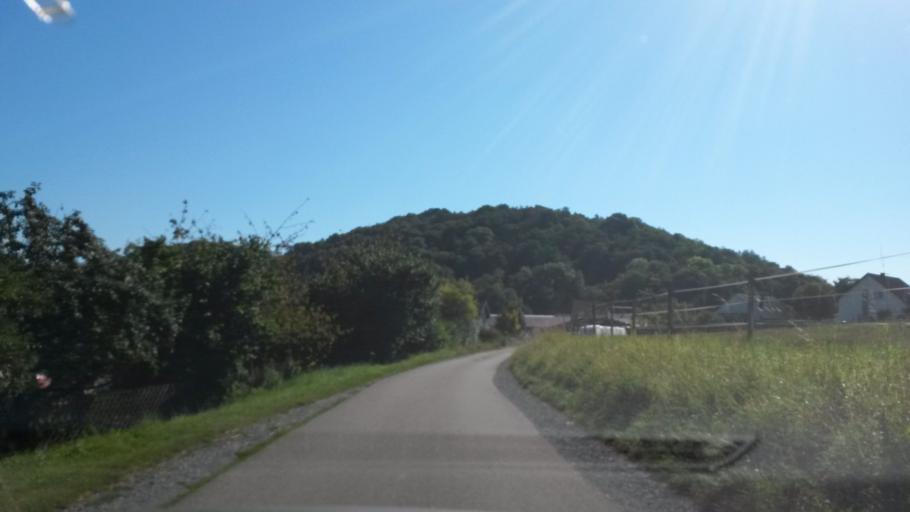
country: DE
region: Baden-Wuerttemberg
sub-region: Karlsruhe Region
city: Eisingen
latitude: 48.9582
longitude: 8.6387
